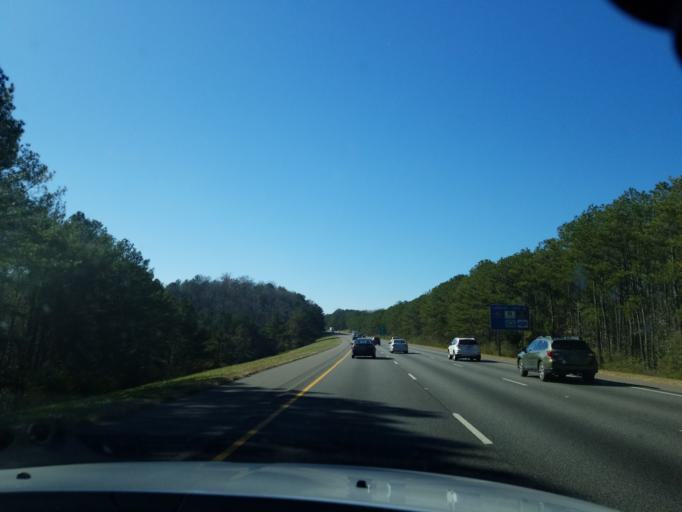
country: US
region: Alabama
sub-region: Jefferson County
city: Hoover
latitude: 33.3710
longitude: -86.8356
